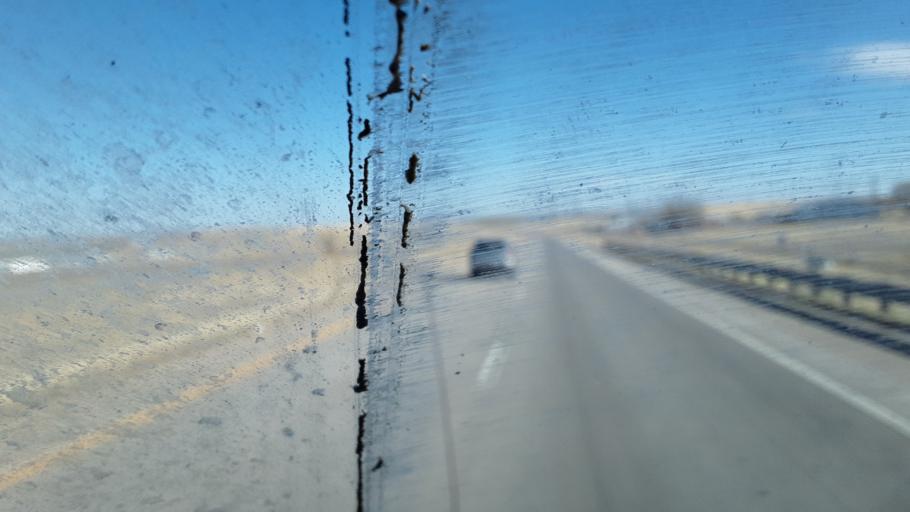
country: US
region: Colorado
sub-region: Weld County
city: Keenesburg
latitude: 40.1101
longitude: -104.5641
